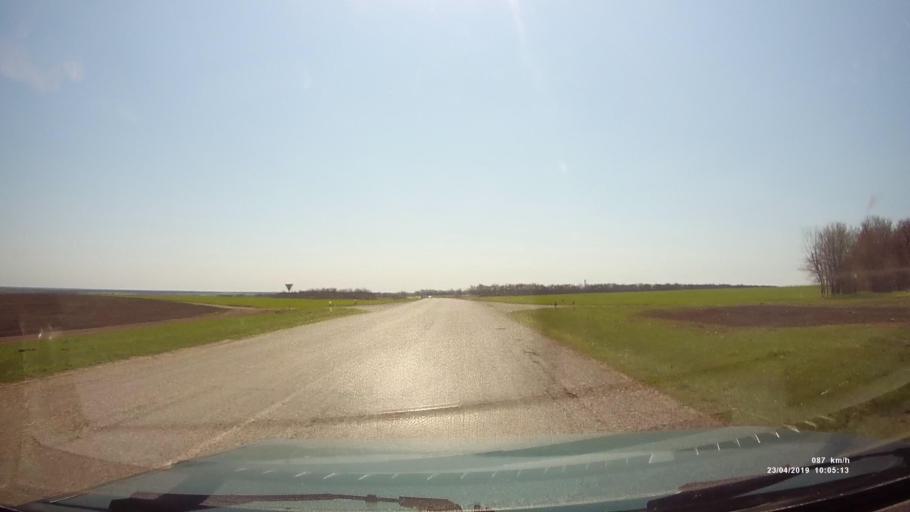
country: RU
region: Rostov
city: Sovetskoye
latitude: 46.7440
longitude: 42.2147
